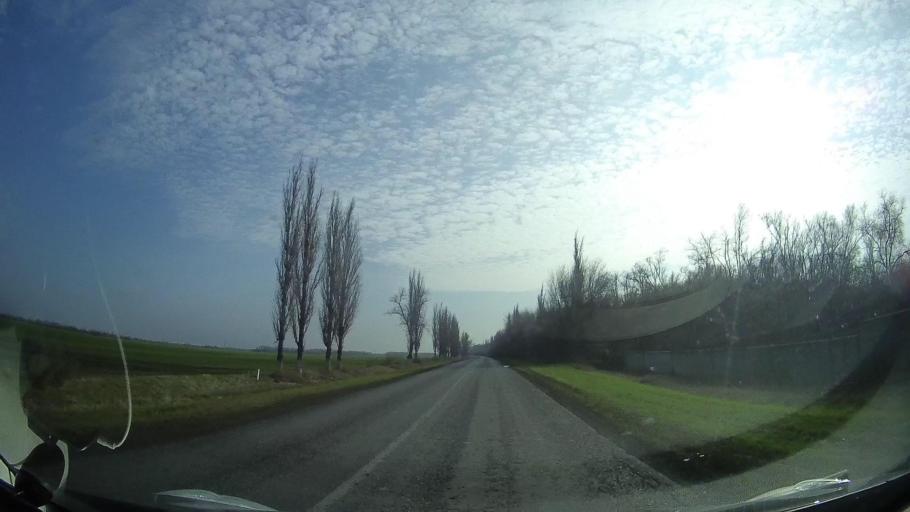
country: RU
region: Rostov
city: Mechetinskaya
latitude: 46.8274
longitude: 40.5525
